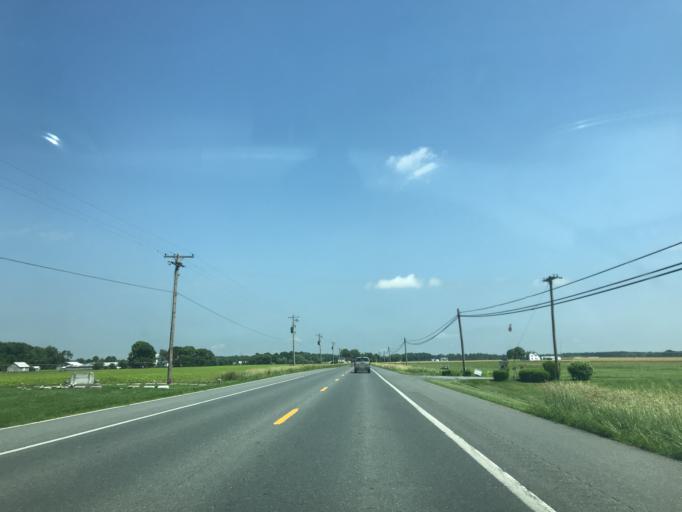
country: US
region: Maryland
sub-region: Dorchester County
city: Hurlock
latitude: 38.5814
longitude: -75.8496
